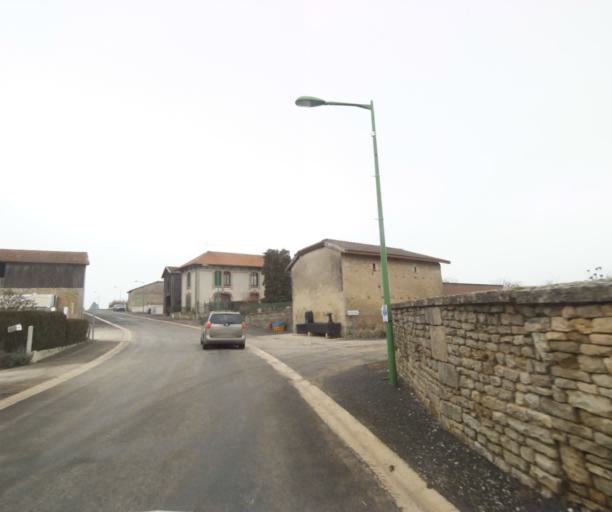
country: FR
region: Champagne-Ardenne
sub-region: Departement de la Haute-Marne
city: Chevillon
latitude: 48.4944
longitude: 5.0670
